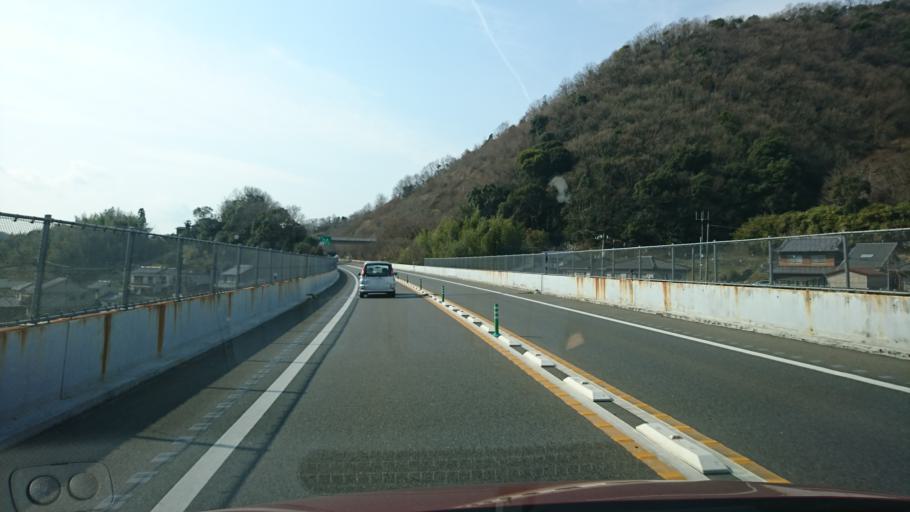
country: JP
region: Hiroshima
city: Onomichi
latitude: 34.3850
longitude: 133.1972
